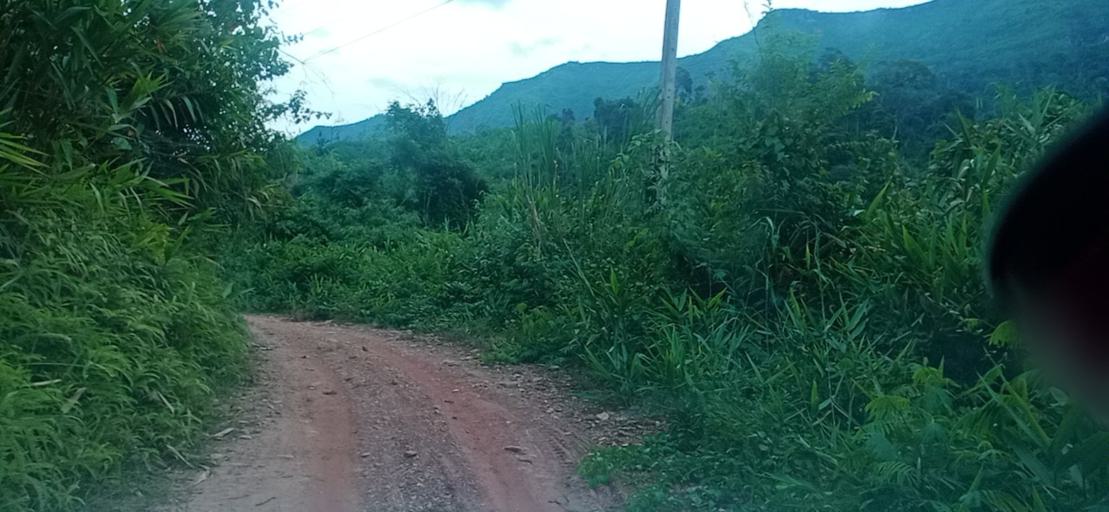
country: TH
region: Changwat Bueng Kan
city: Pak Khat
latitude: 18.5603
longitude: 103.2551
